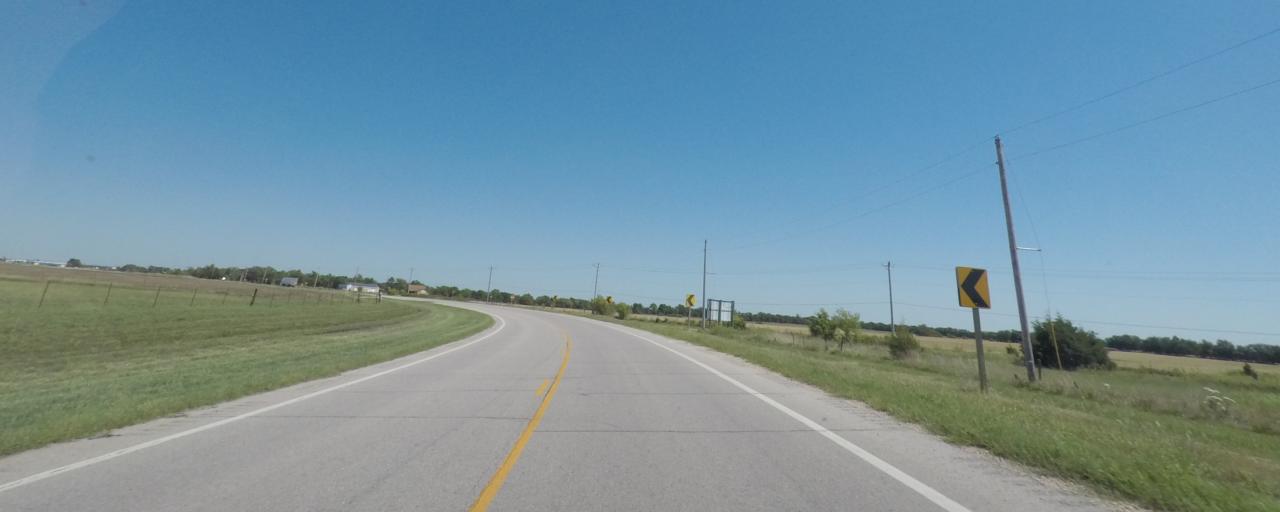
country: US
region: Kansas
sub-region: Sumner County
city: Wellington
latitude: 37.3068
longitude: -97.3859
